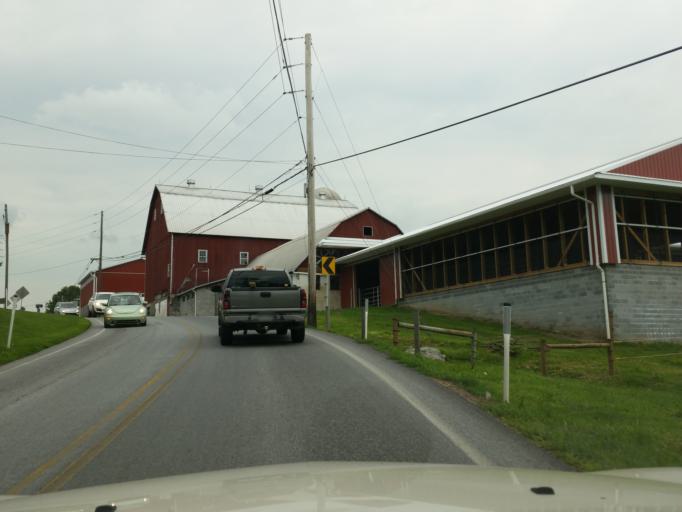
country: US
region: Pennsylvania
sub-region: Lancaster County
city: Strasburg
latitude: 39.9955
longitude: -76.2047
